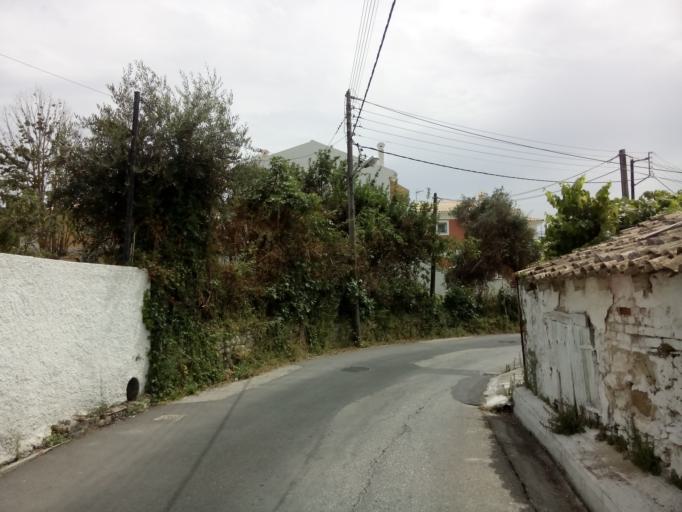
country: GR
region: Ionian Islands
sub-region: Nomos Kerkyras
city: Perama
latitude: 39.5965
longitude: 19.9182
